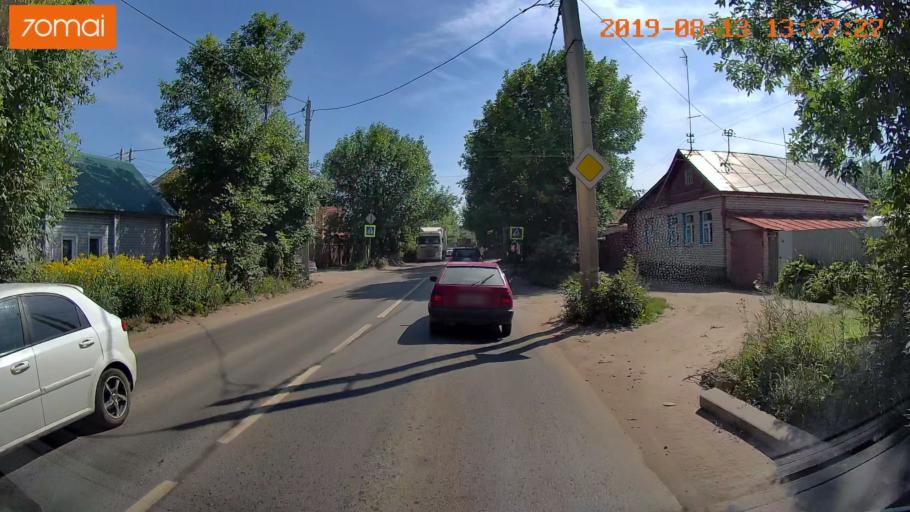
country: RU
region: Ivanovo
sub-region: Gorod Ivanovo
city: Ivanovo
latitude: 56.9950
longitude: 40.9517
